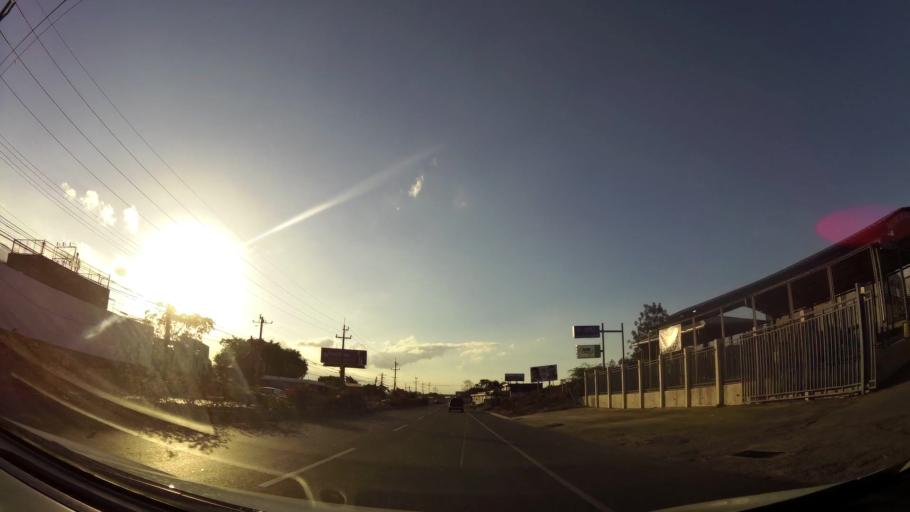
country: DO
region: Santiago
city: Palmar Arriba
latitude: 19.5003
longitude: -70.7428
